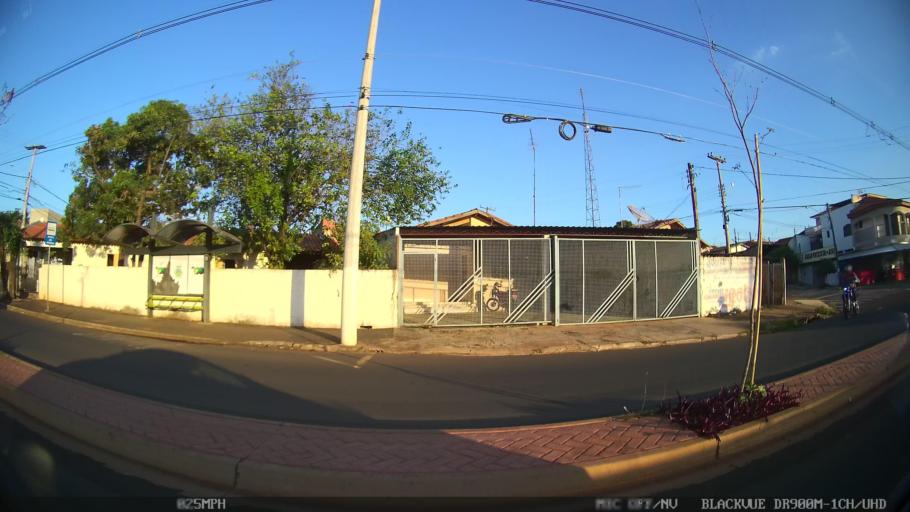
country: BR
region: Sao Paulo
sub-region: Santa Barbara D'Oeste
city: Santa Barbara d'Oeste
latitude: -22.7406
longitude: -47.4013
